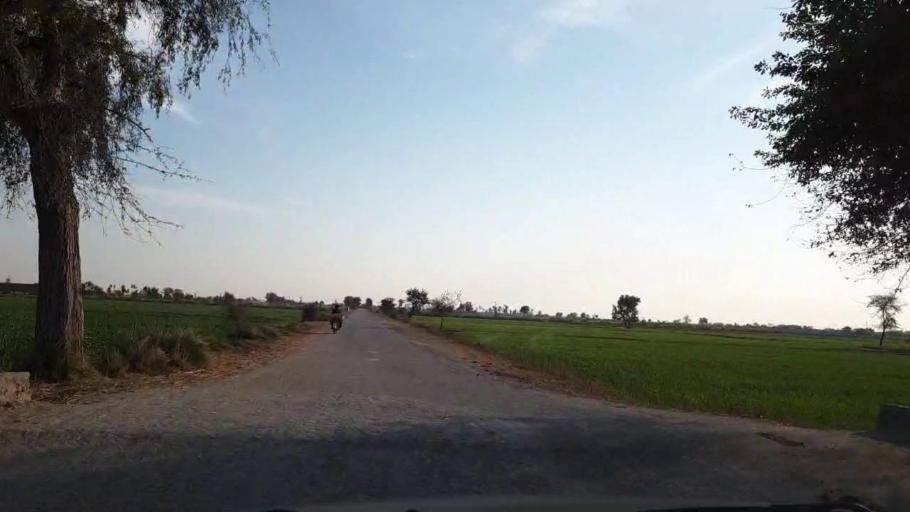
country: PK
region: Sindh
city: Khadro
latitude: 26.1667
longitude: 68.7532
